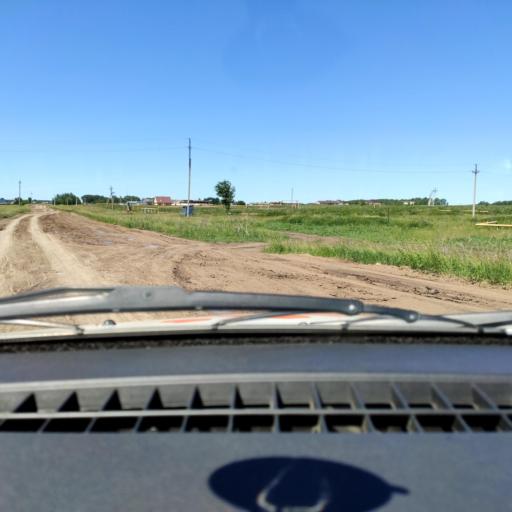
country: RU
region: Bashkortostan
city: Avdon
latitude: 54.5090
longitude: 55.7901
